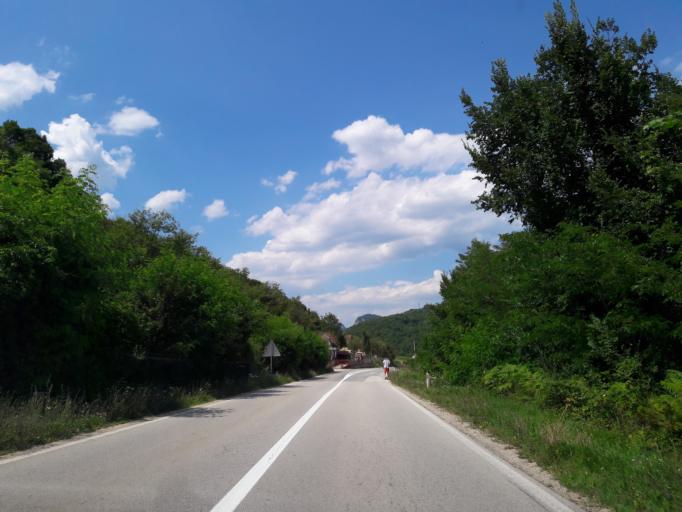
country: BA
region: Republika Srpska
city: Mrkonjic Grad
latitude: 44.5345
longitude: 17.1498
